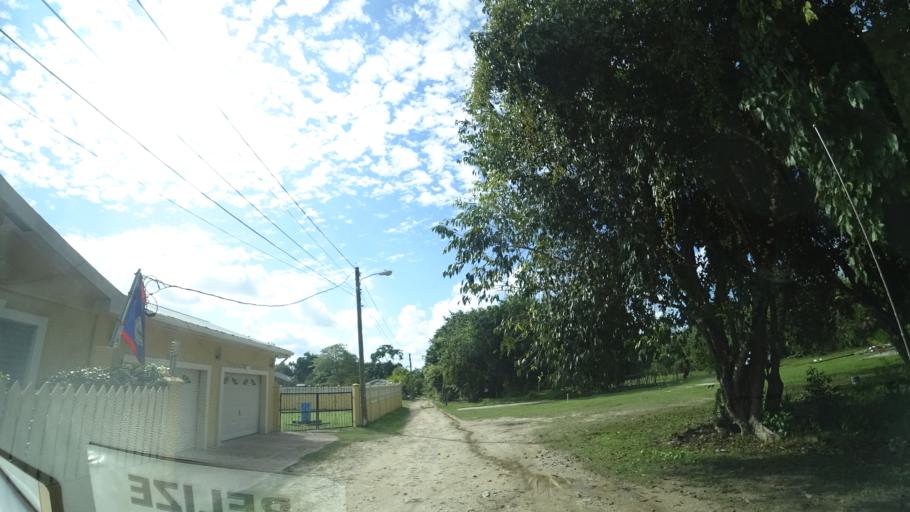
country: BZ
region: Belize
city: Belize City
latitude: 17.5589
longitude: -88.4066
